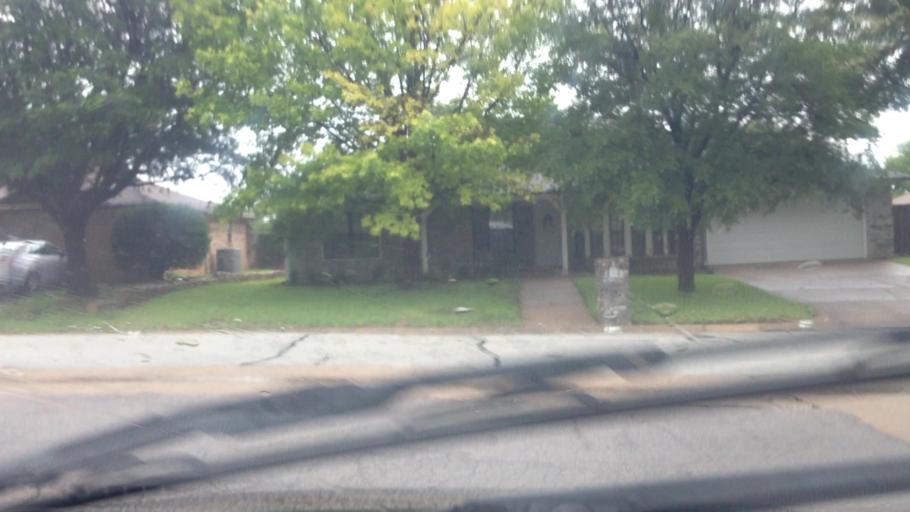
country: US
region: Texas
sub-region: Tarrant County
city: Watauga
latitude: 32.8813
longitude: -97.2268
